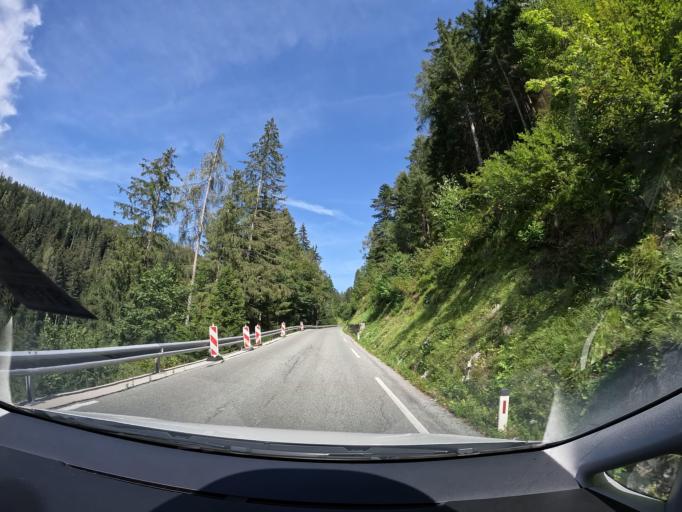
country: AT
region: Carinthia
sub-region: Politischer Bezirk Villach Land
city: Sankt Jakob
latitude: 46.5404
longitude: 14.0863
